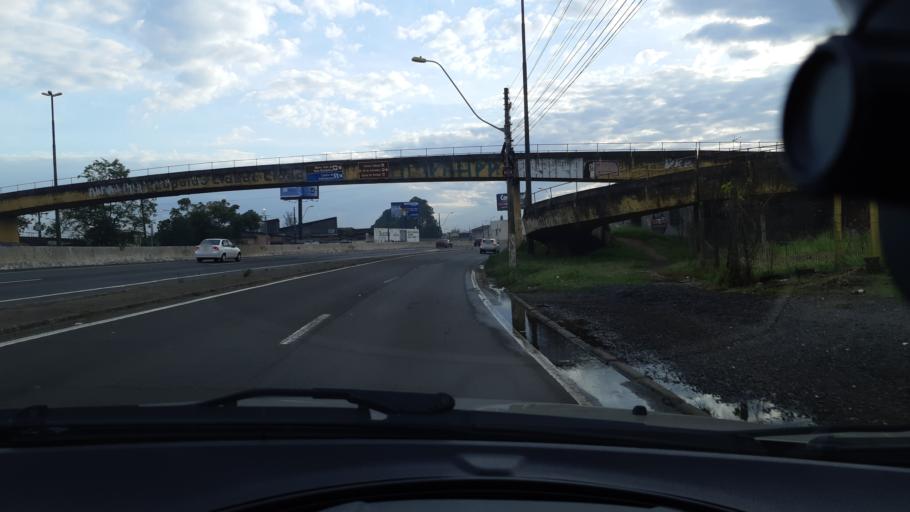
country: BR
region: Rio Grande do Sul
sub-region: Sao Leopoldo
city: Sao Leopoldo
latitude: -29.7653
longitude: -51.1538
